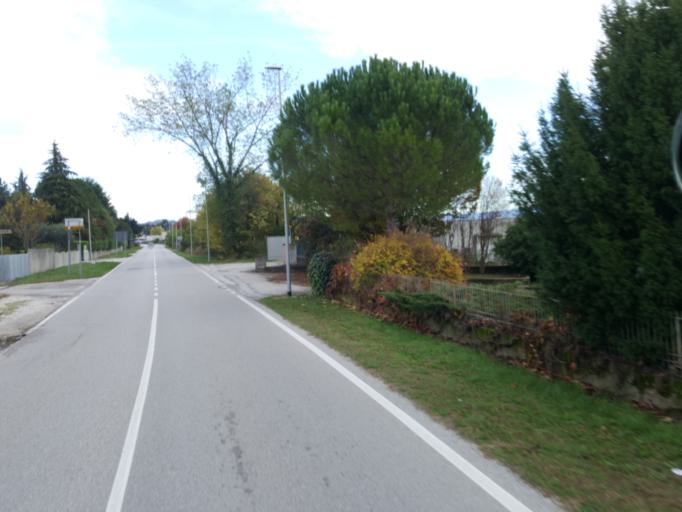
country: IT
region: Friuli Venezia Giulia
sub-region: Provincia di Udine
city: Manzano
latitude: 45.9825
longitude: 13.3662
